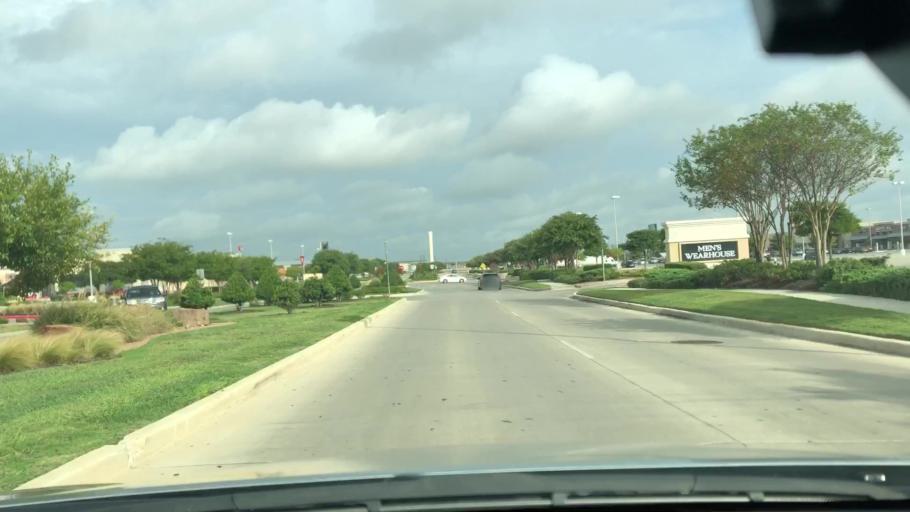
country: US
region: Texas
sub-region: Guadalupe County
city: Lake Dunlap
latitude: 29.7282
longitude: -98.0723
